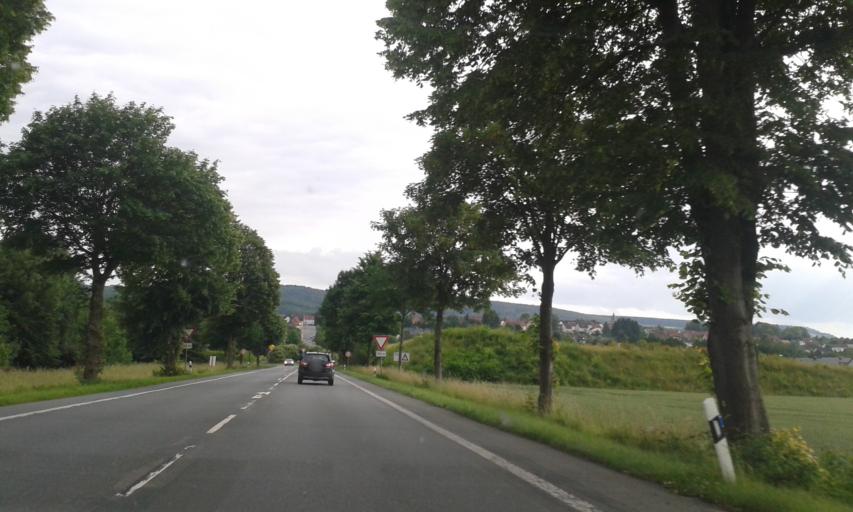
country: DE
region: North Rhine-Westphalia
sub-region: Regierungsbezirk Detmold
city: Barntrup
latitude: 51.9993
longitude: 9.1224
